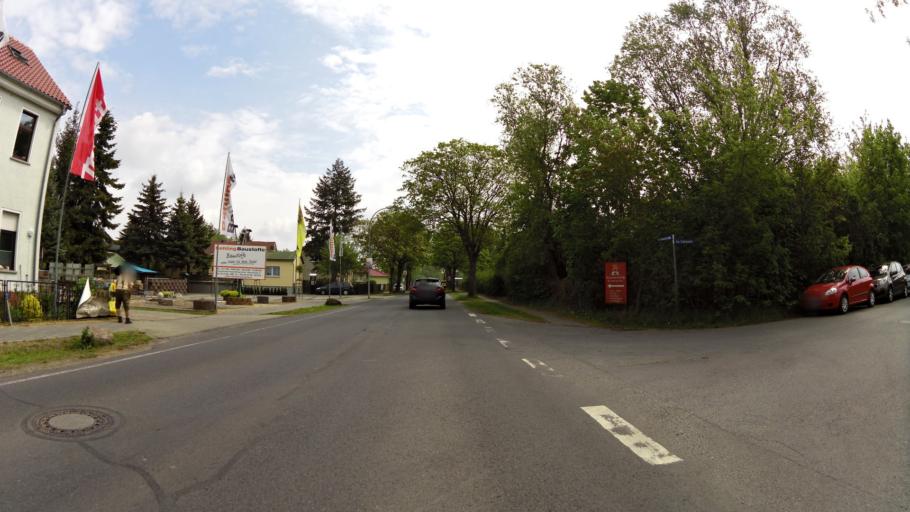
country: DE
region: Brandenburg
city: Mittenwalde
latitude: 52.2600
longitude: 13.5478
